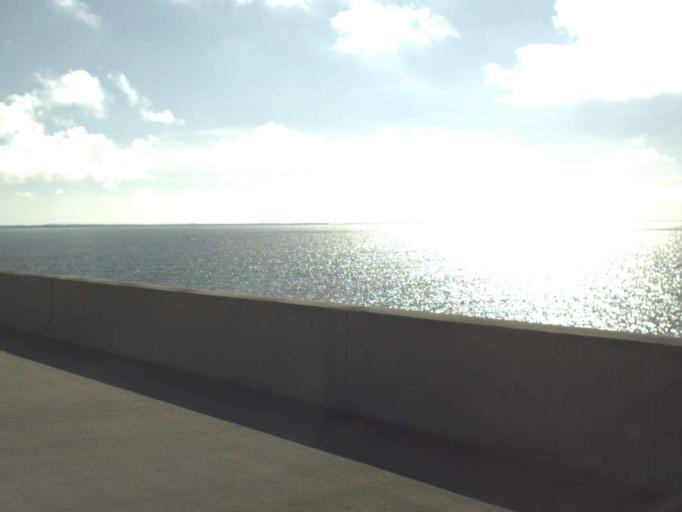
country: US
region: Florida
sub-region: Franklin County
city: Eastpoint
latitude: 29.7081
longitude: -84.8907
